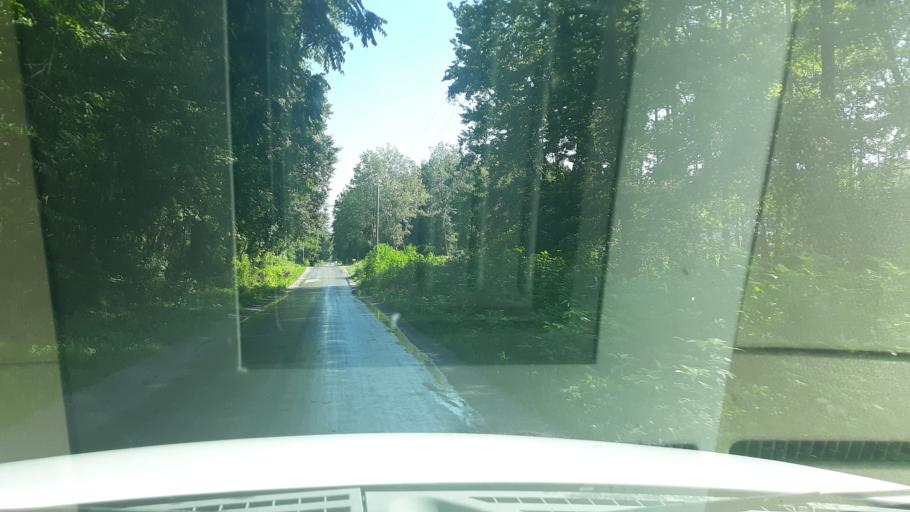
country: US
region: Illinois
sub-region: Saline County
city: Harrisburg
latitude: 37.8592
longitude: -88.5814
